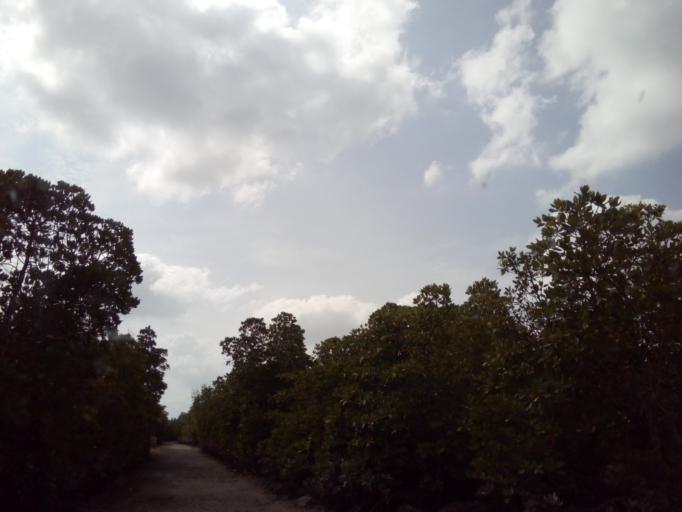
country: TZ
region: Zanzibar Central/South
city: Mahonda
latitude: -6.3185
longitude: 39.3870
